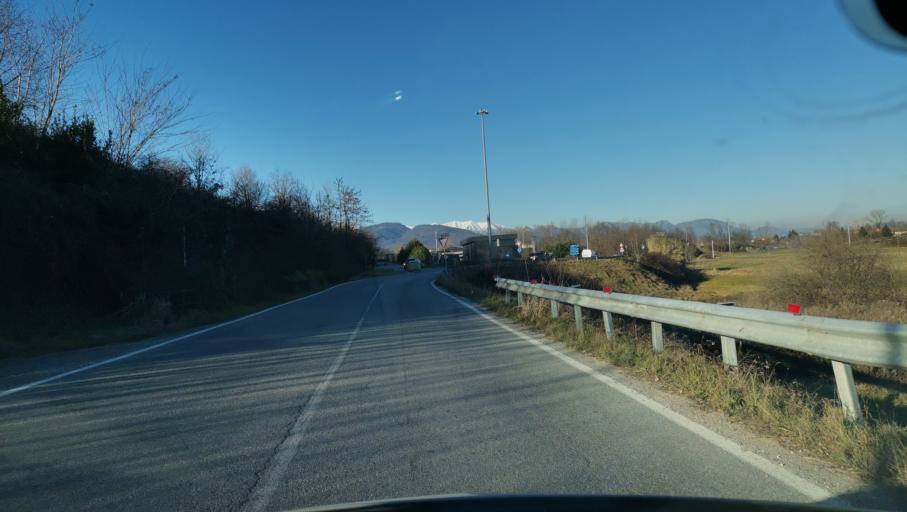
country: IT
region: Piedmont
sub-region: Provincia di Torino
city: Bibiana
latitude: 44.7883
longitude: 7.2935
